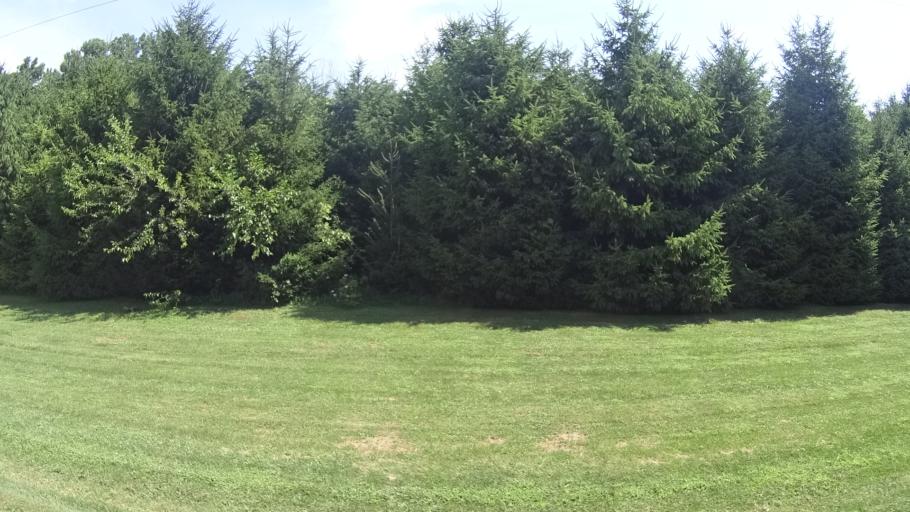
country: US
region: Ohio
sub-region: Erie County
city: Sandusky
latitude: 41.4137
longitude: -82.8058
